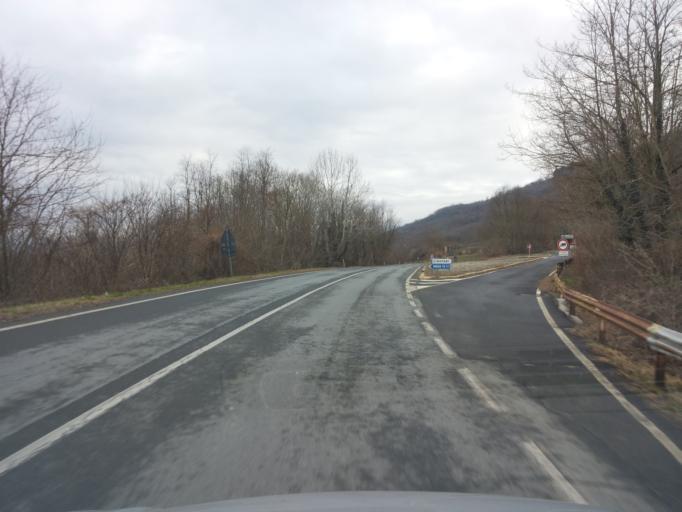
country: IT
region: Piedmont
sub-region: Provincia di Torino
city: Vestigne
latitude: 45.3790
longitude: 7.9669
